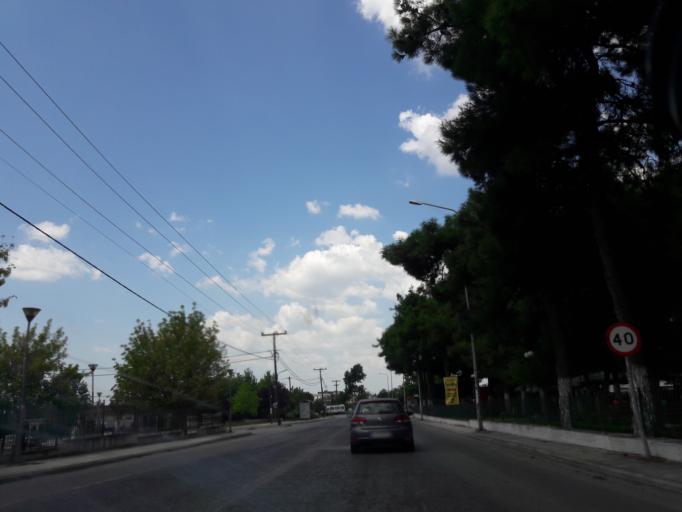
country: GR
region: Central Macedonia
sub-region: Nomos Thessalonikis
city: Thermi
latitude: 40.5253
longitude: 23.0489
